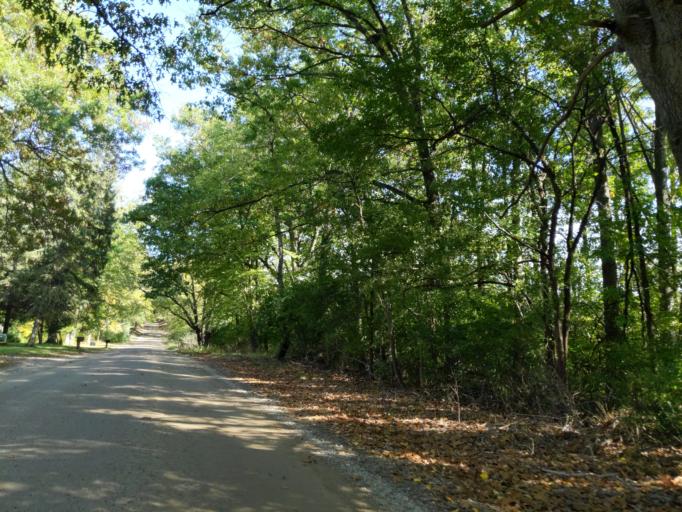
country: US
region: Michigan
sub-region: Clinton County
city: Bath
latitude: 42.8059
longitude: -84.4400
